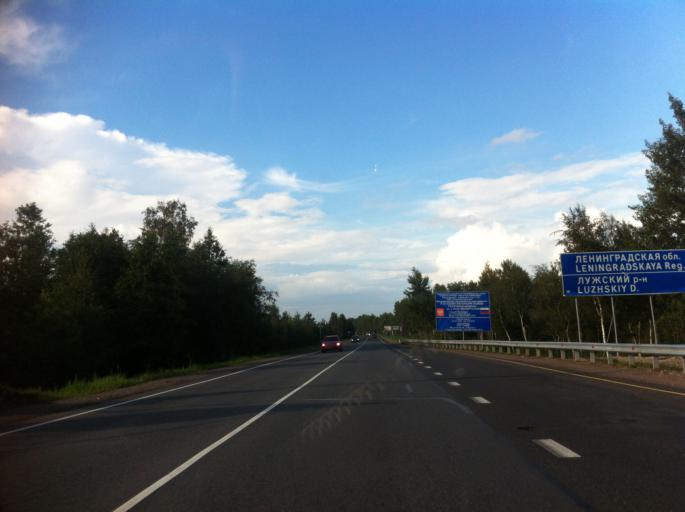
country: RU
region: Leningrad
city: Luga
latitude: 58.4366
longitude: 29.7478
